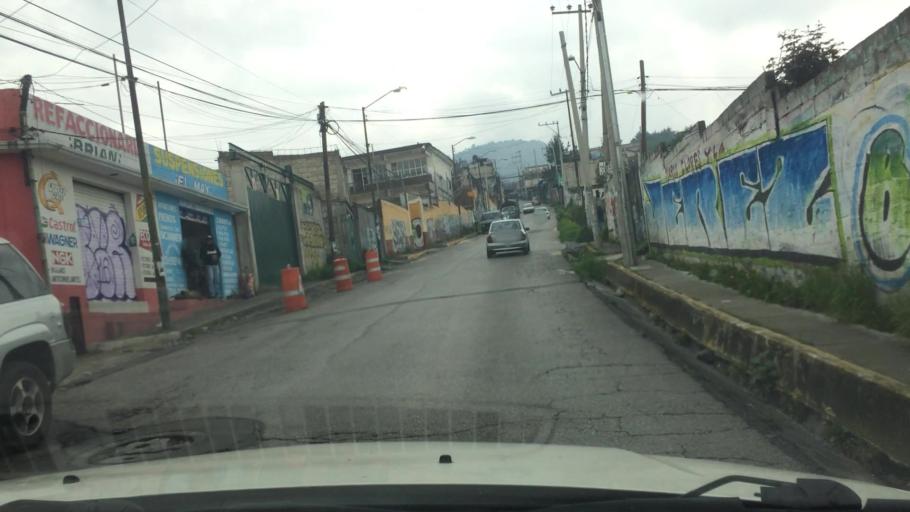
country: MX
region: Mexico City
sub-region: Tlalpan
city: Lomas de Tepemecatl
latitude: 19.2267
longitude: -99.2000
